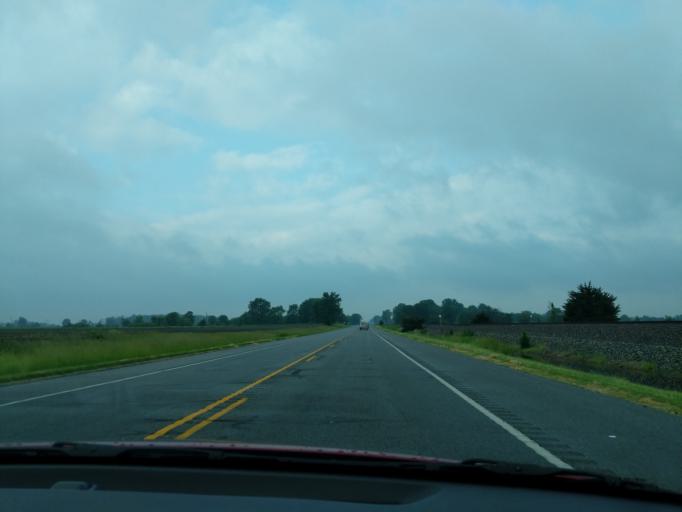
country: US
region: Indiana
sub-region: Hancock County
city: Fortville
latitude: 39.9163
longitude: -85.8815
